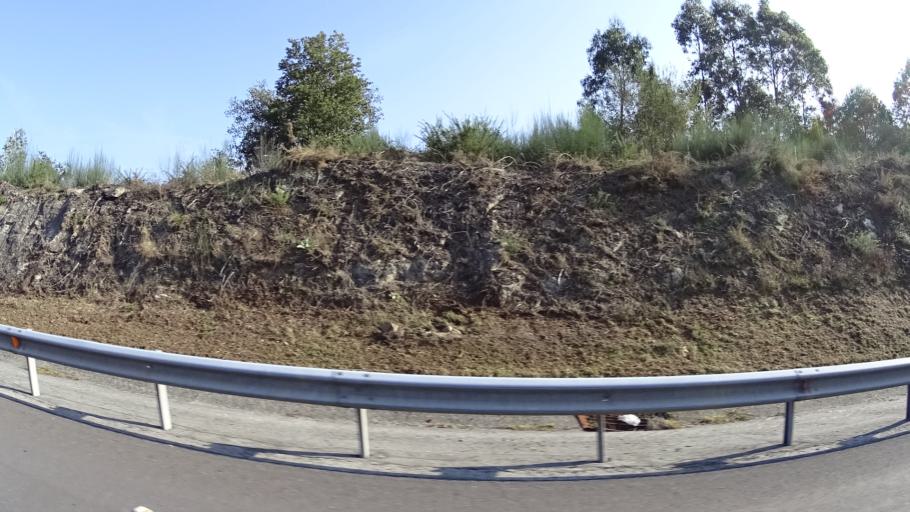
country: ES
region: Galicia
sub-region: Provincia da Coruna
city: Coiros
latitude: 43.2443
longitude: -8.1456
